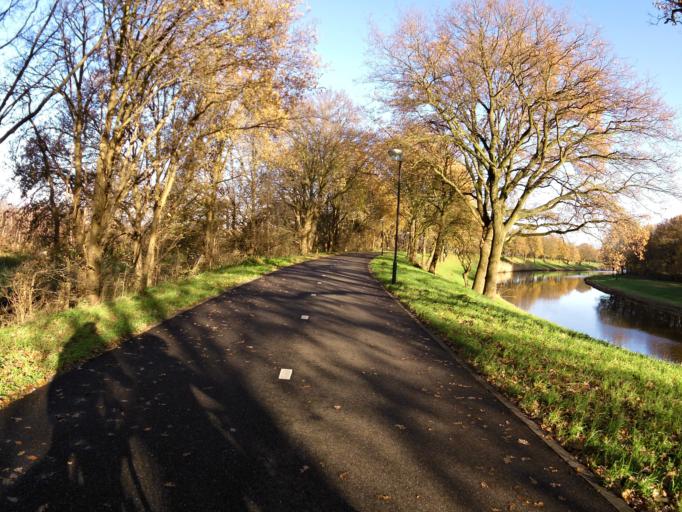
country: NL
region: North Brabant
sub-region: Gemeente Vught
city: Vught
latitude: 51.6744
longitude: 5.2838
